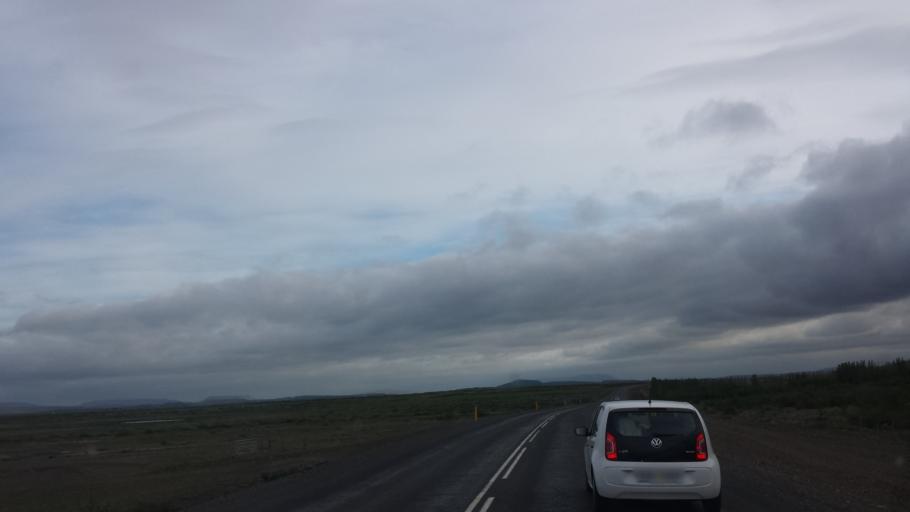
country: IS
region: South
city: Selfoss
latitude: 64.2852
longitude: -20.3409
